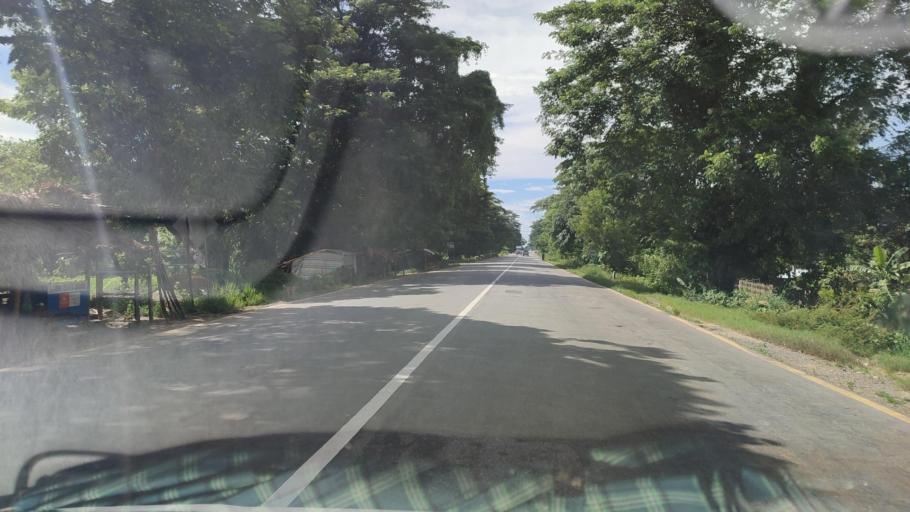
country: MM
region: Bago
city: Pyu
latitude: 18.3048
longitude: 96.5081
